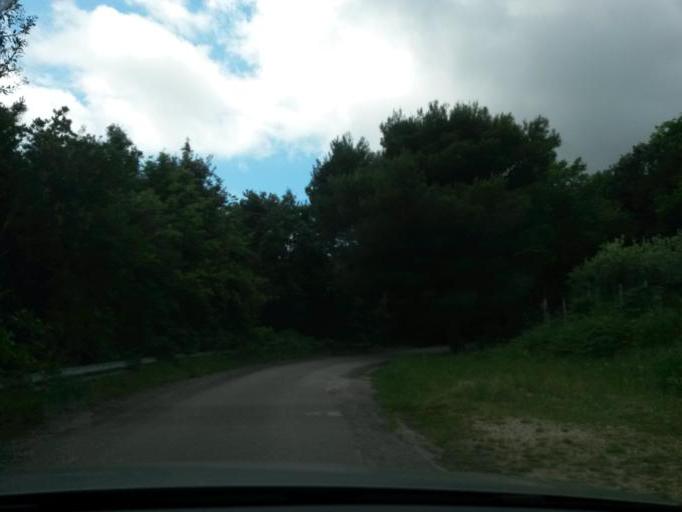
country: IT
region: Tuscany
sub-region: Provincia di Livorno
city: Campo nell'Elba
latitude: 42.7618
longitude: 10.2036
